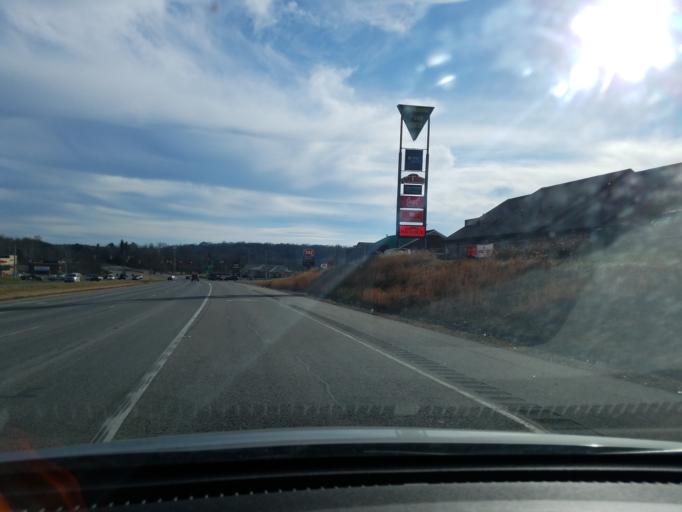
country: US
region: Indiana
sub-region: Floyd County
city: Galena
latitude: 38.3150
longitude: -85.8982
